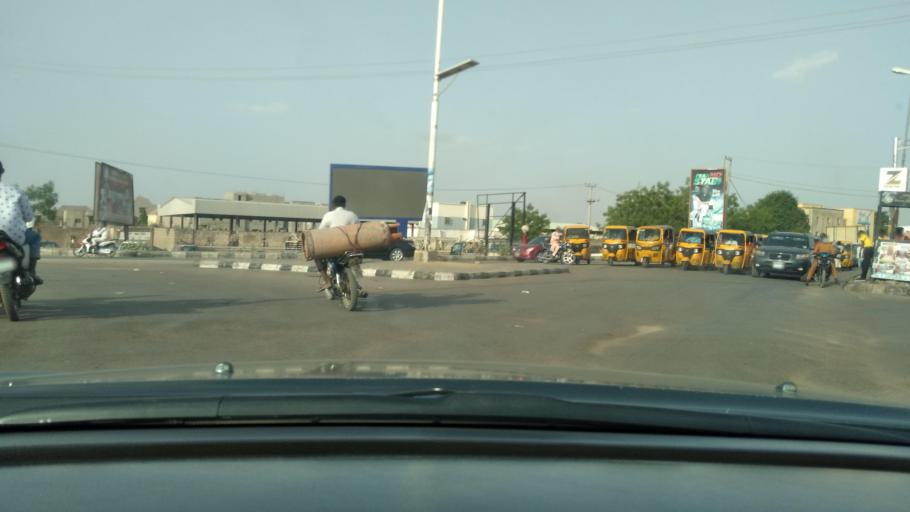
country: NG
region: Kano
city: Kano
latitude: 11.9765
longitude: 8.5652
